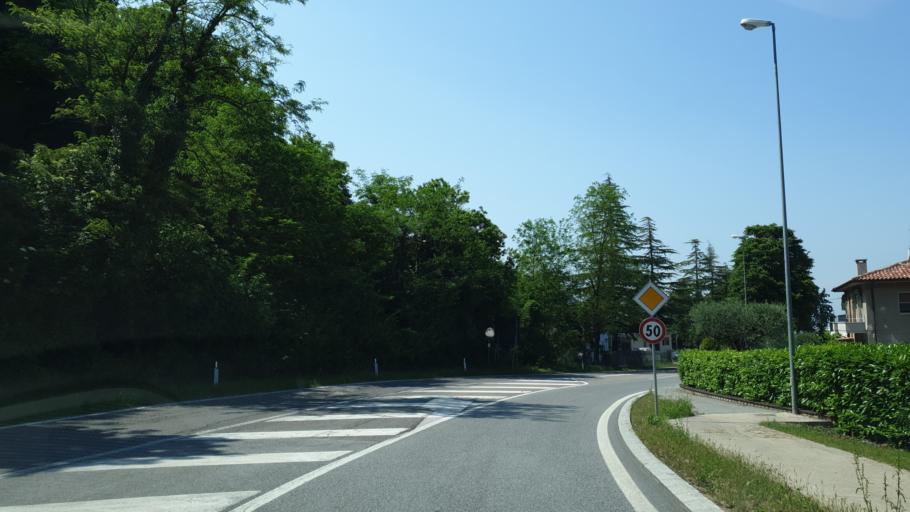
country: SM
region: Acquaviva
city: Acquaviva
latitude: 43.9429
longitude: 12.4316
